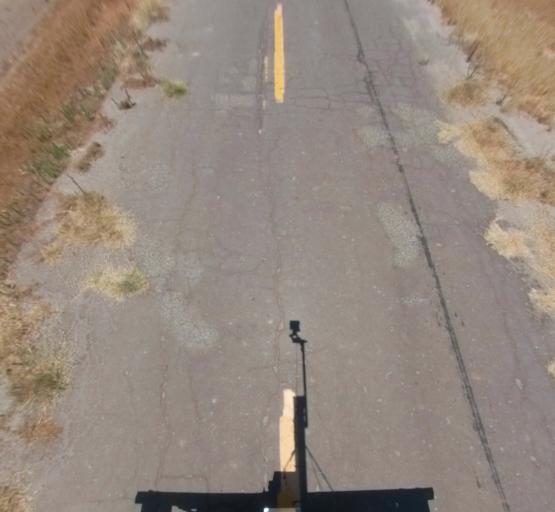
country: US
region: California
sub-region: Madera County
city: Fairmead
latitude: 37.0237
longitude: -120.2206
